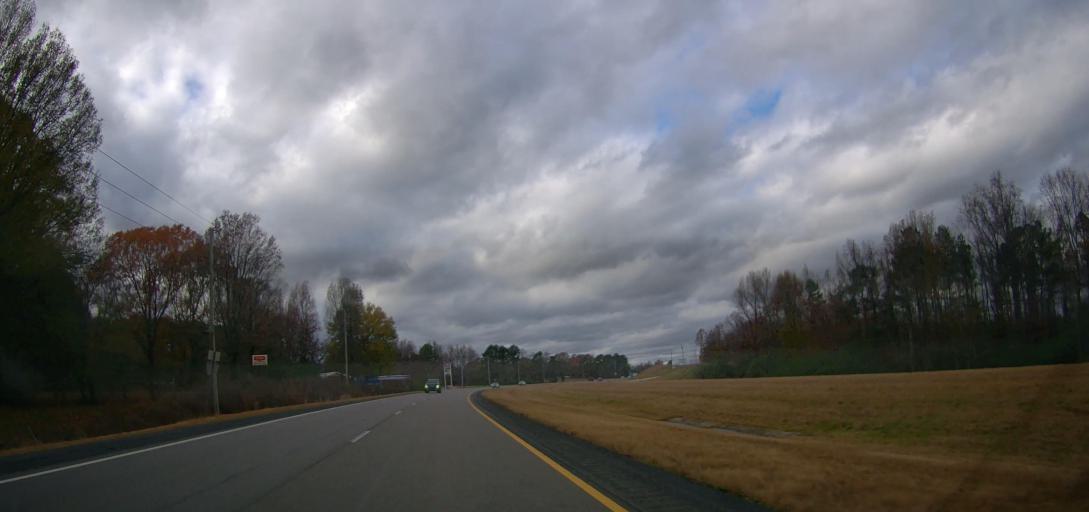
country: US
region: Alabama
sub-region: Morgan County
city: Falkville
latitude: 34.2630
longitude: -86.9872
